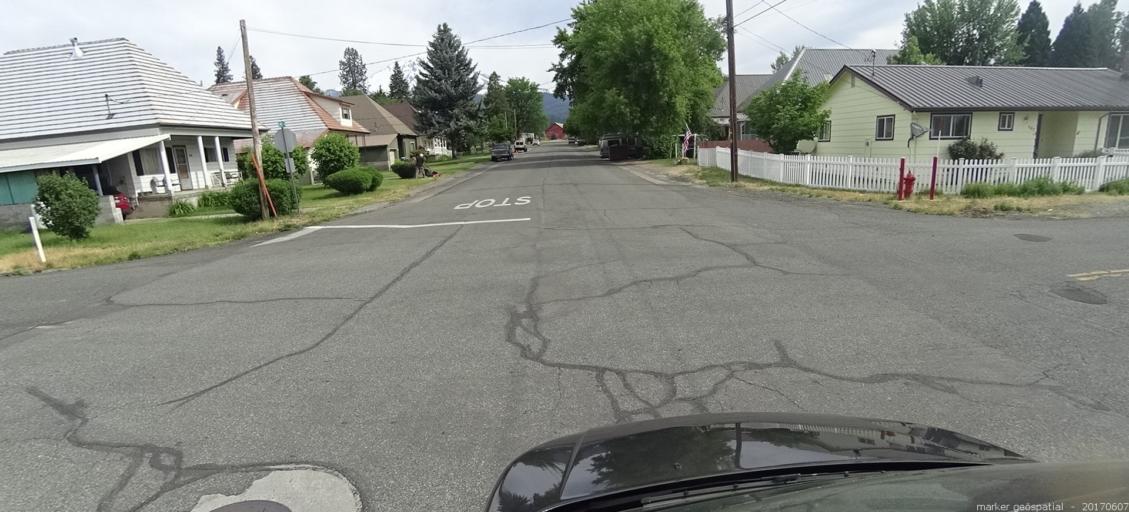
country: US
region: California
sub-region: Siskiyou County
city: McCloud
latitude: 41.2559
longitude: -122.1378
